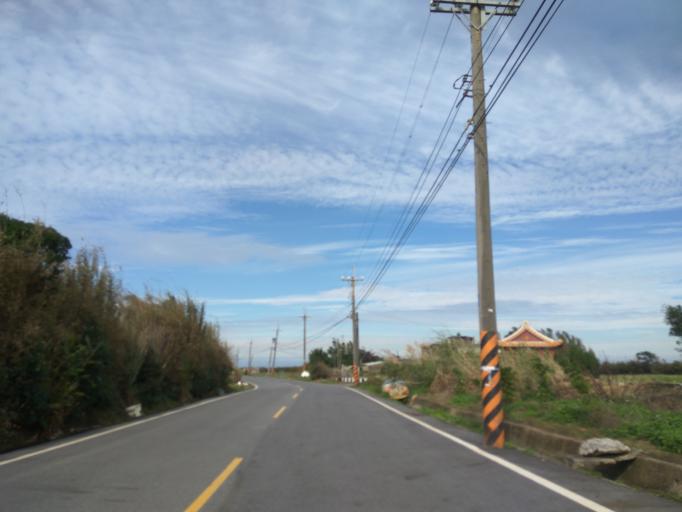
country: TW
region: Taiwan
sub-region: Hsinchu
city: Zhubei
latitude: 25.0025
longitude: 121.0858
